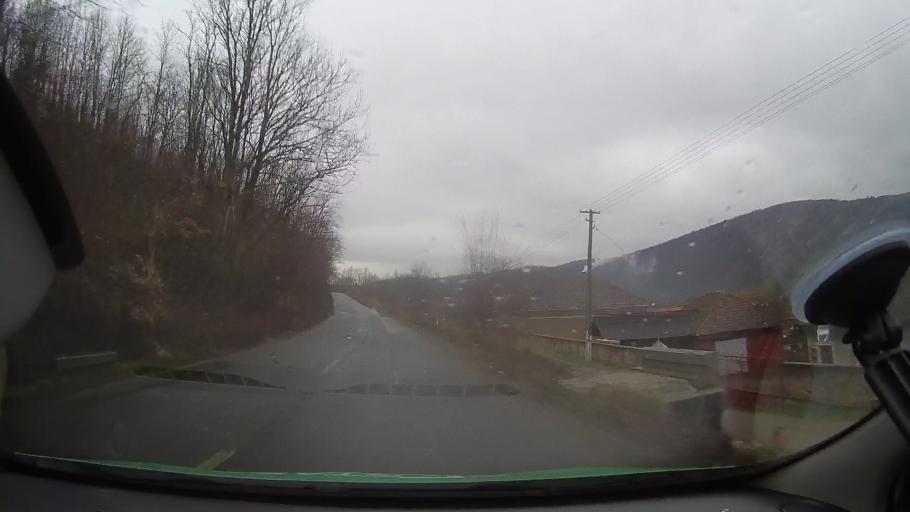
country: RO
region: Arad
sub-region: Comuna Halmagiu
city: Halmagiu
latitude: 46.2376
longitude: 22.5581
